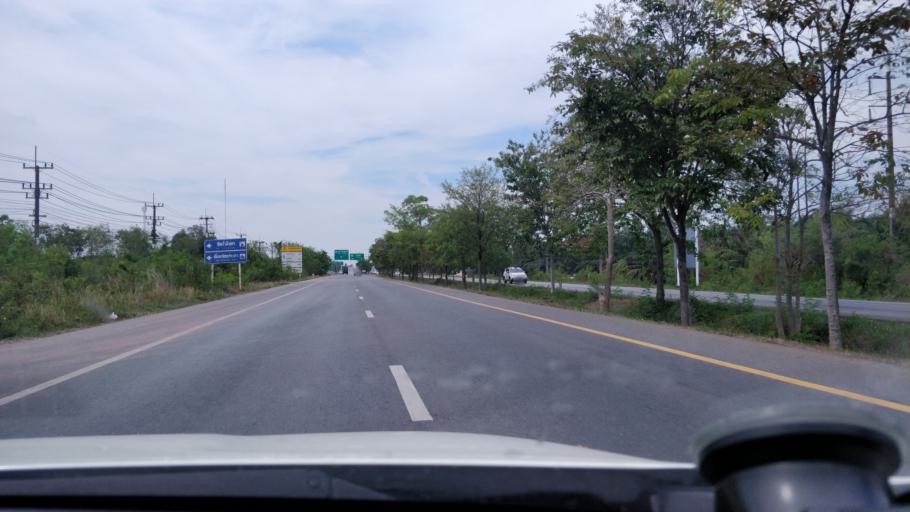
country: TH
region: Surat Thani
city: Phunphin
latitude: 9.0447
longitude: 99.1727
